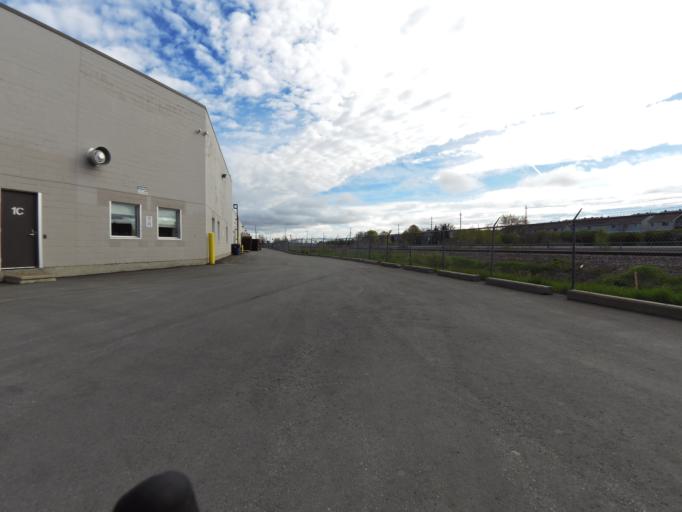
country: CA
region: Ontario
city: Bells Corners
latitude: 45.2927
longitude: -75.7421
